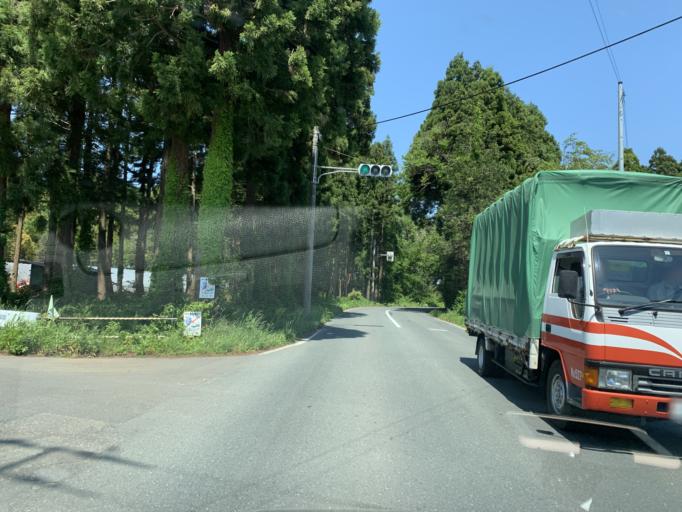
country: JP
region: Iwate
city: Kitakami
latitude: 39.2662
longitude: 141.0587
